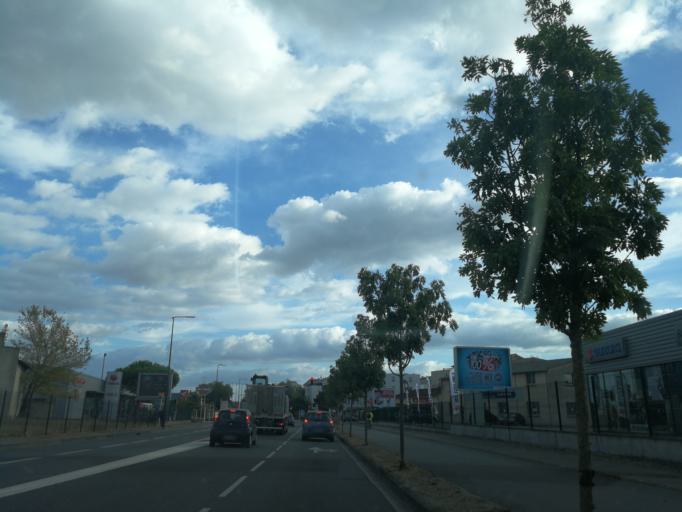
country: FR
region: Midi-Pyrenees
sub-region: Departement de la Haute-Garonne
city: L'Union
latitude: 43.6370
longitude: 1.4724
